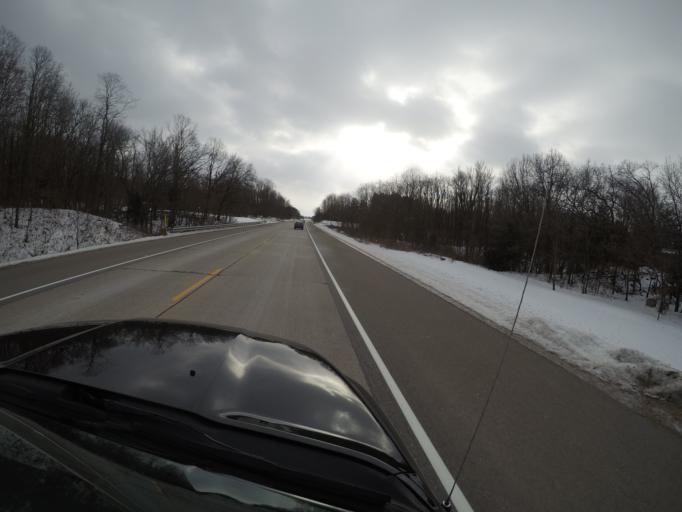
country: US
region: Wisconsin
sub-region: Trempealeau County
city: Galesville
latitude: 44.0413
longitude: -91.2907
